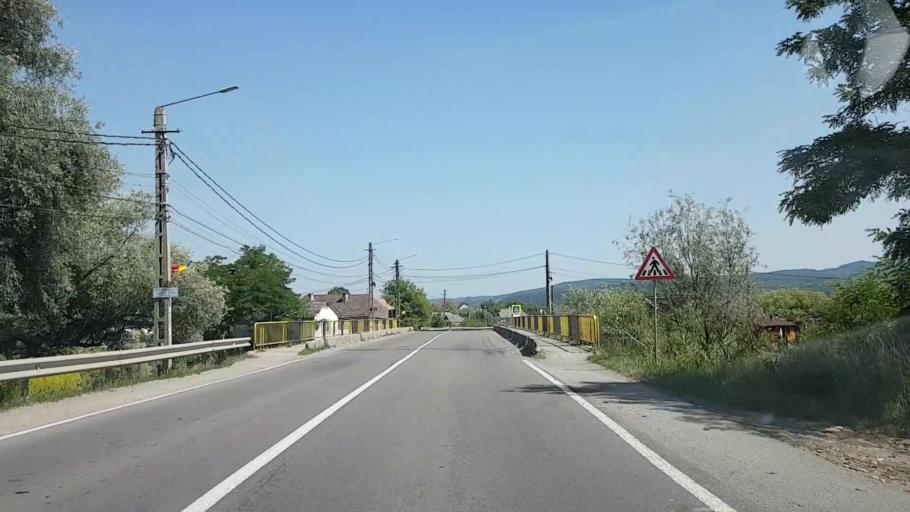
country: RO
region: Bistrita-Nasaud
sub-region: Comuna Uriu
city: Cristestii Ciceului
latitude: 47.1929
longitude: 24.0955
